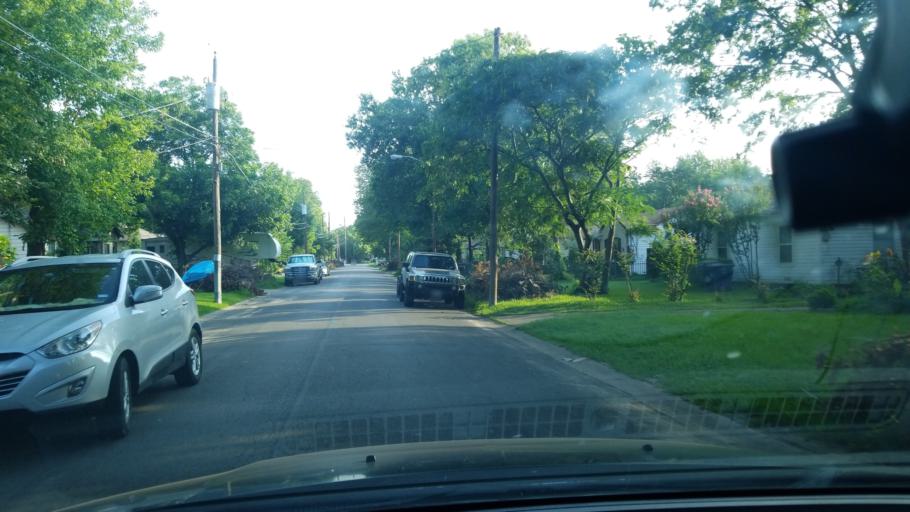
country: US
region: Texas
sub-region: Dallas County
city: Balch Springs
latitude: 32.7175
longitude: -96.6778
